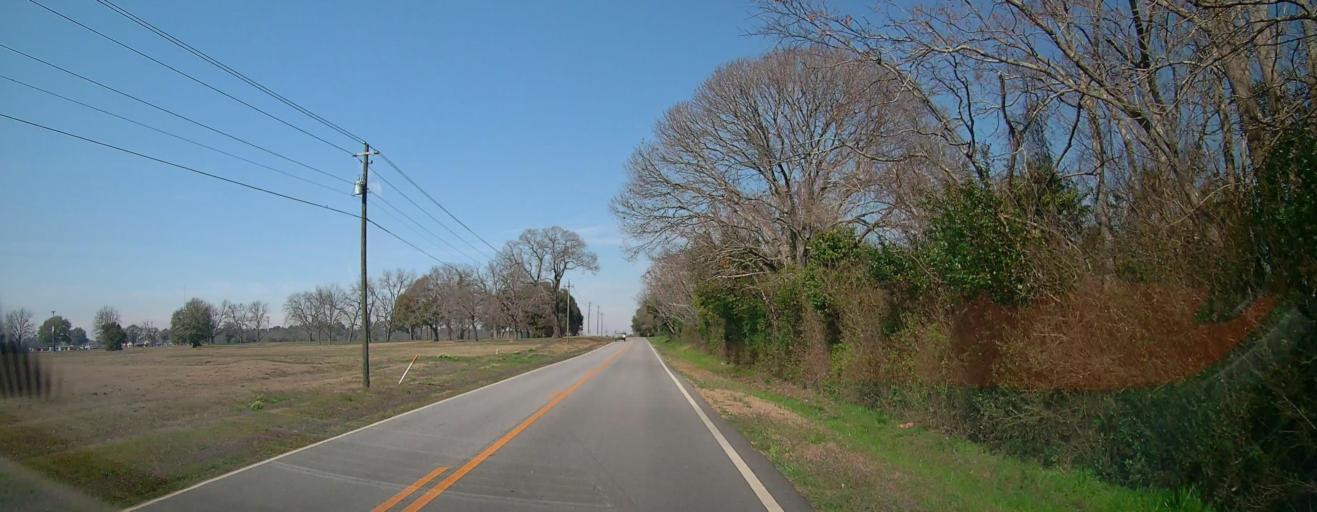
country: US
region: Georgia
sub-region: Houston County
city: Perry
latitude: 32.4365
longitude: -83.7367
